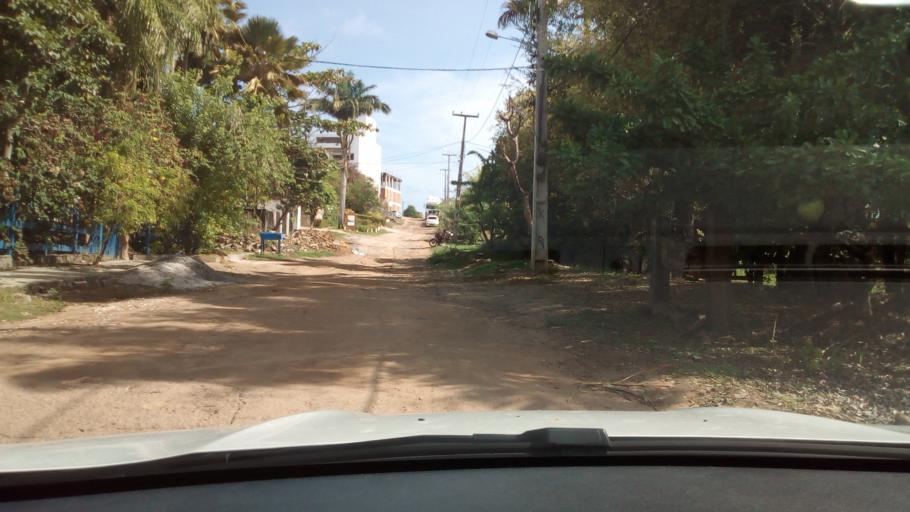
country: BR
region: Paraiba
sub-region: Conde
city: Conde
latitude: -7.2990
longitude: -34.8009
